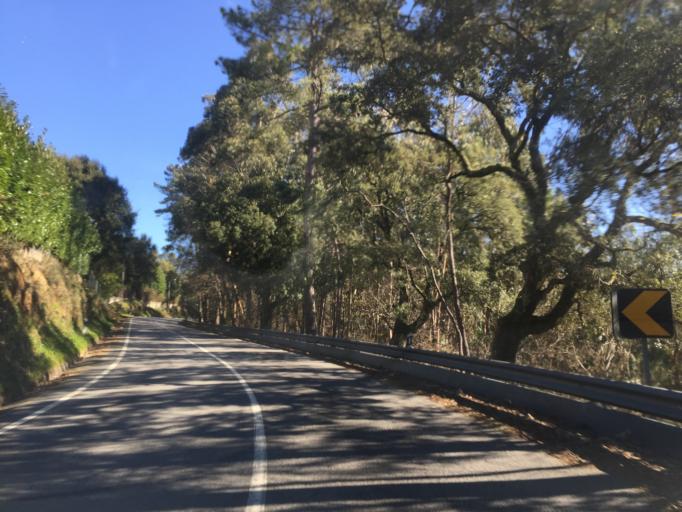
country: PT
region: Aveiro
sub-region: Vale de Cambra
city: Macieira de Cambra
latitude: 40.8878
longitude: -8.3511
